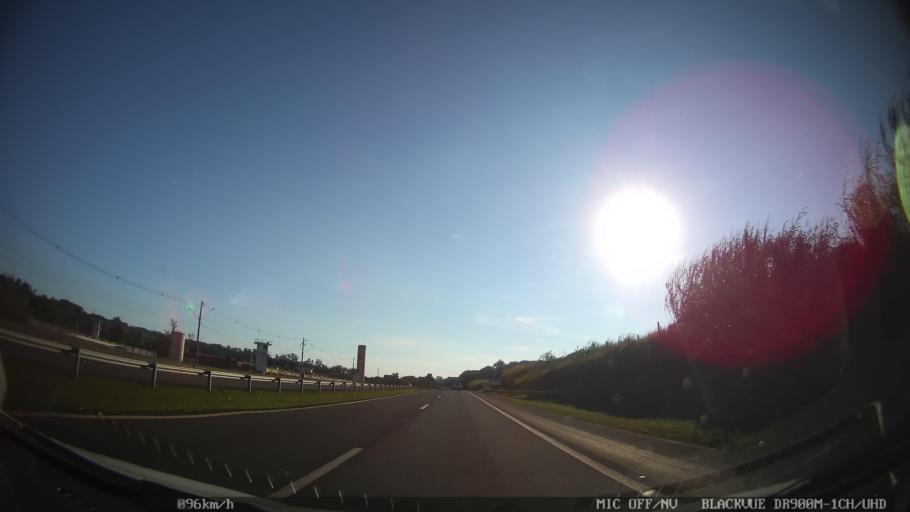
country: BR
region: Sao Paulo
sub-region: Piracicaba
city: Piracicaba
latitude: -22.6982
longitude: -47.6103
